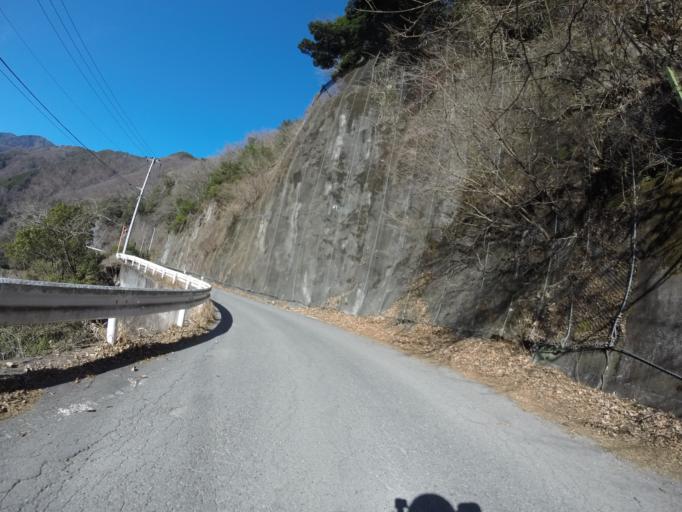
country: JP
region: Yamanashi
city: Ryuo
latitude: 35.4121
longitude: 138.3547
